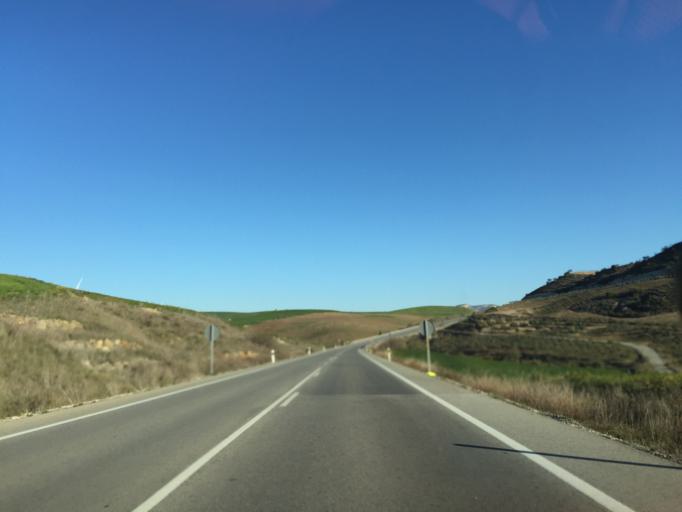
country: ES
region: Andalusia
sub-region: Provincia de Malaga
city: Ardales
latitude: 36.9059
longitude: -4.8409
